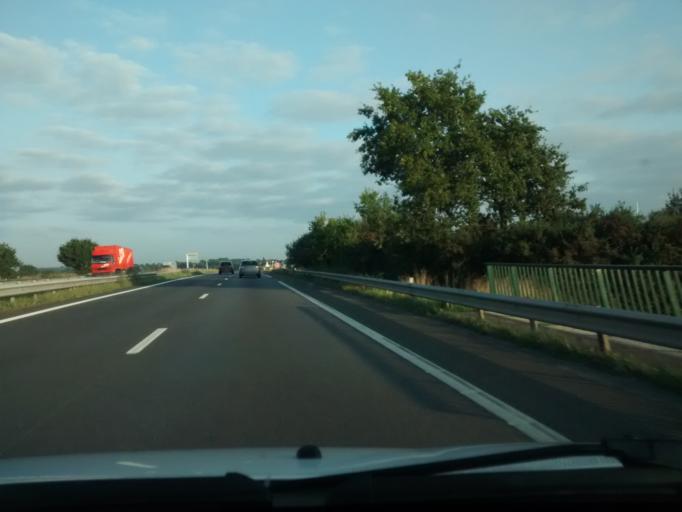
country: FR
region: Brittany
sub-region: Departement des Cotes-d'Armor
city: Lamballe
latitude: 48.4674
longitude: -2.5486
